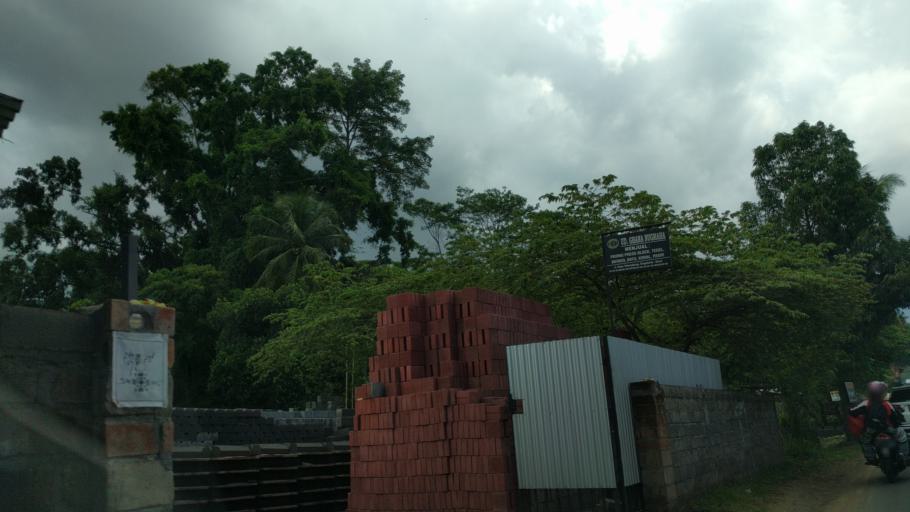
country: ID
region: Bali
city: Banjar Tebongkang
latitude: -8.5307
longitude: 115.2440
